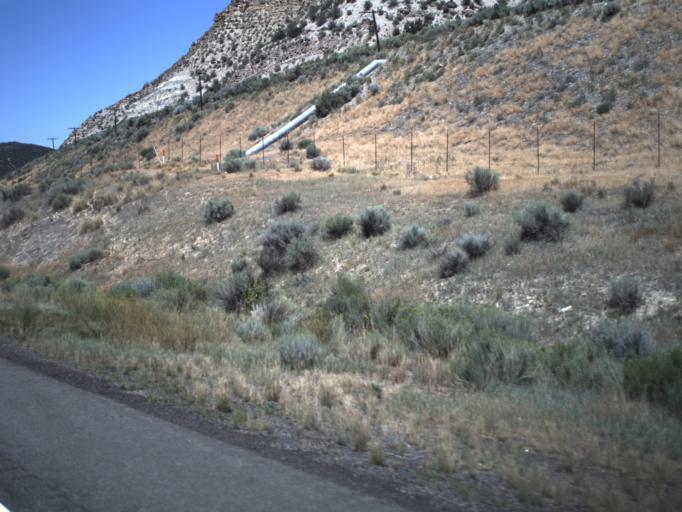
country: US
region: Utah
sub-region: Sanpete County
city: Fairview
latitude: 39.9290
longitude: -111.1830
